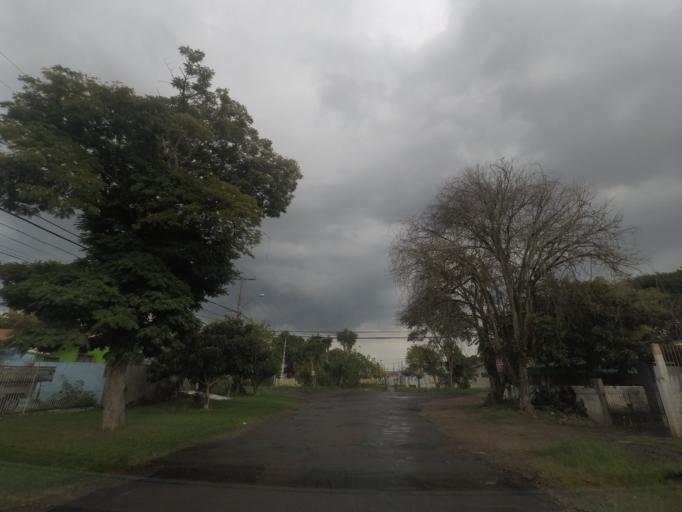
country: BR
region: Parana
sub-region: Sao Jose Dos Pinhais
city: Sao Jose dos Pinhais
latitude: -25.4844
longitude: -49.2405
